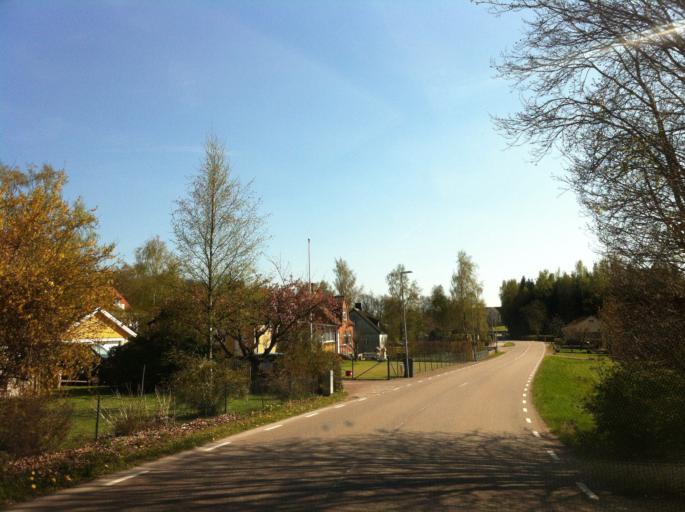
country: SE
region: Skane
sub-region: Svalovs Kommun
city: Kagerod
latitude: 56.0392
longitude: 13.1010
